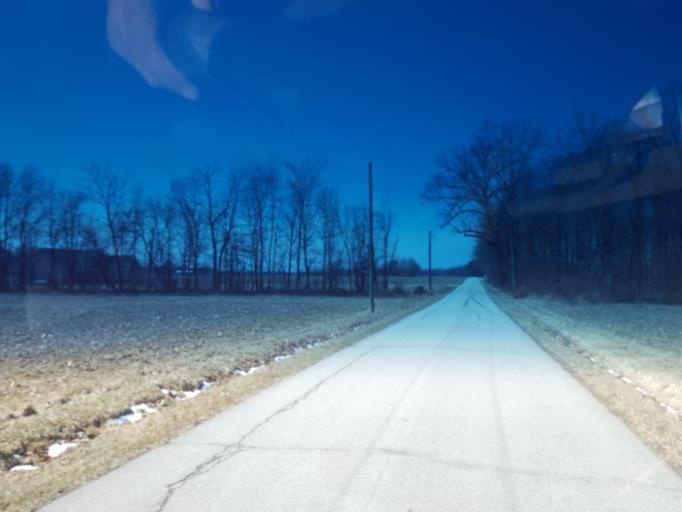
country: US
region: Ohio
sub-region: Crawford County
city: Galion
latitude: 40.7189
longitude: -82.7542
